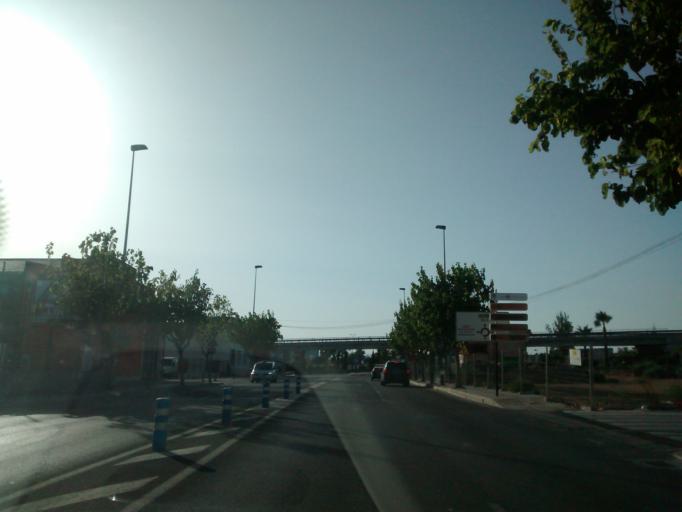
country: ES
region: Valencia
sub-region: Provincia de Alicante
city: Santa Pola
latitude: 38.1992
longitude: -0.5672
